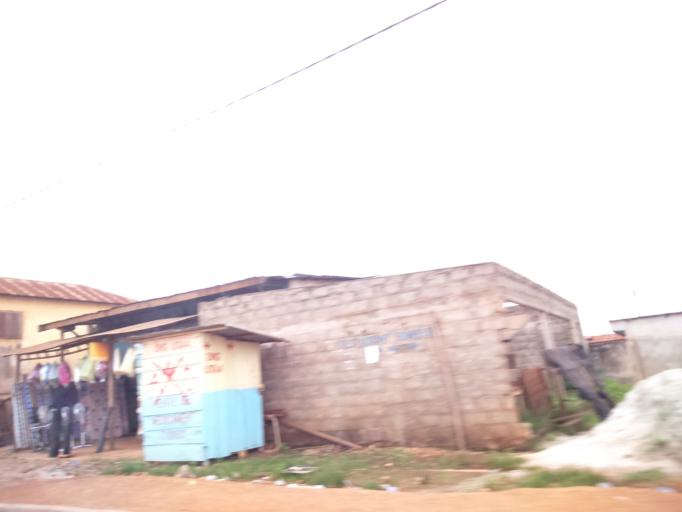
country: CI
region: Moyen-Comoe
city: Abengourou
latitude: 6.7273
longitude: -3.4867
